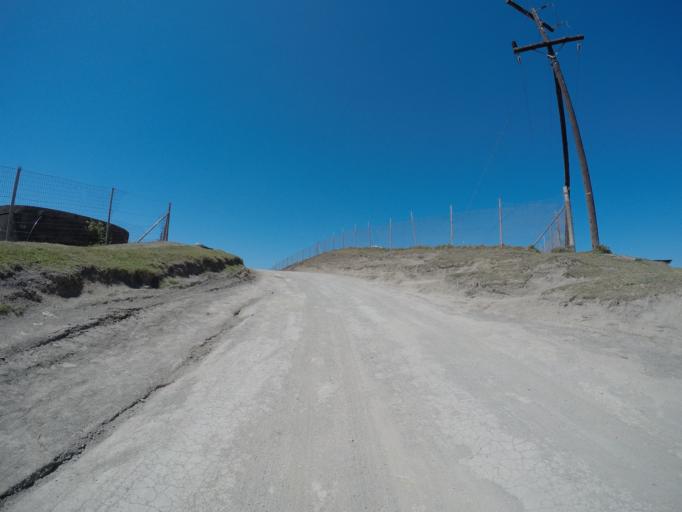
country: ZA
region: Eastern Cape
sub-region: OR Tambo District Municipality
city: Libode
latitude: -32.0330
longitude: 29.1064
